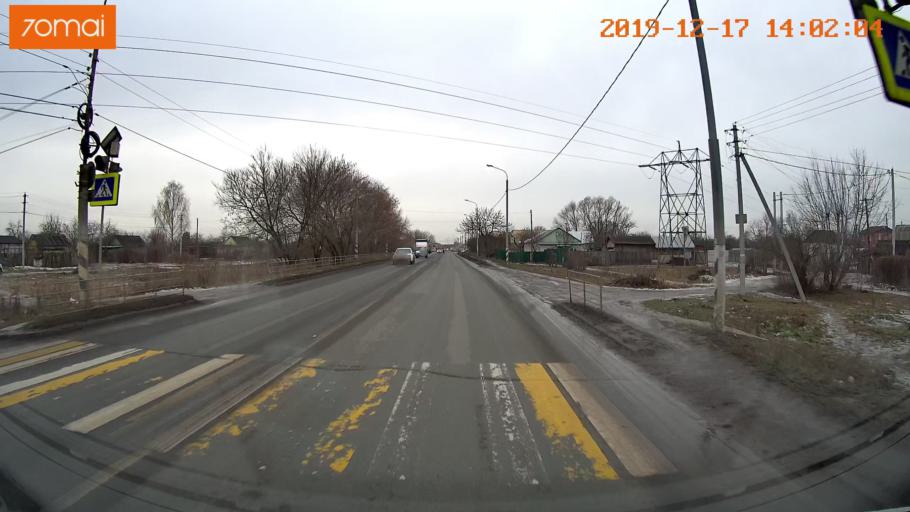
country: RU
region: Rjazan
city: Ryazan'
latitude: 54.6163
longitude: 39.6508
